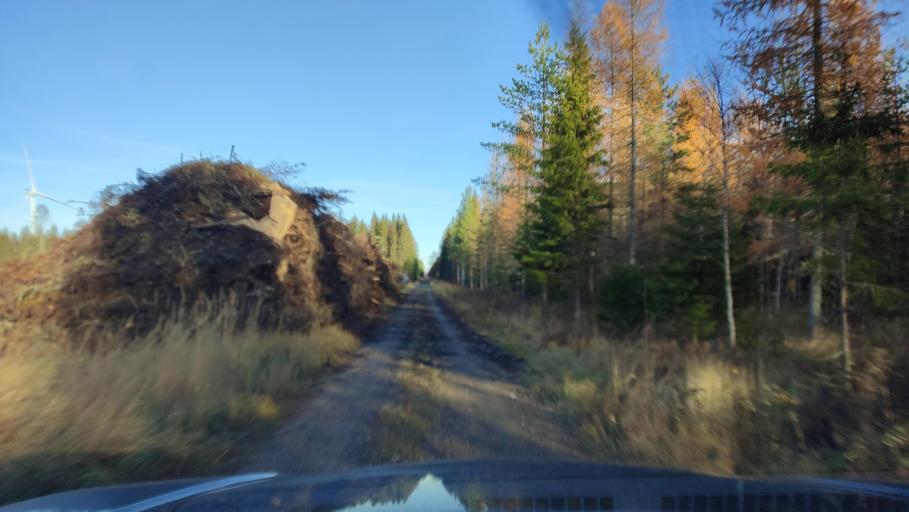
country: FI
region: Southern Ostrobothnia
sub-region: Suupohja
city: Karijoki
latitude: 62.1802
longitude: 21.6090
